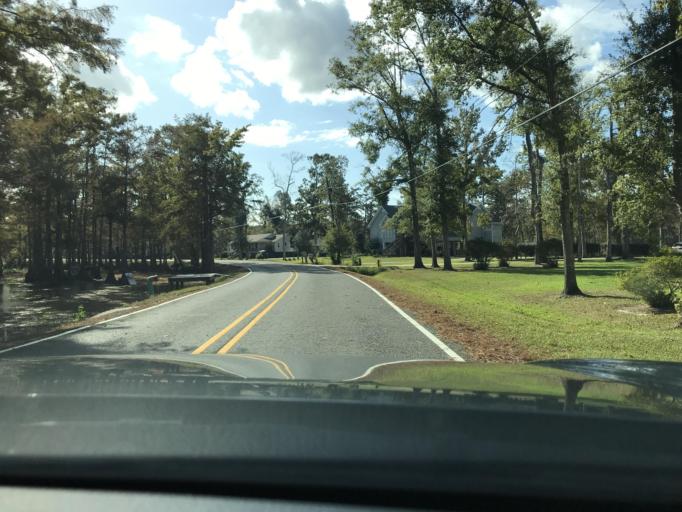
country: US
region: Louisiana
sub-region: Calcasieu Parish
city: Westlake
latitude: 30.3197
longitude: -93.2937
